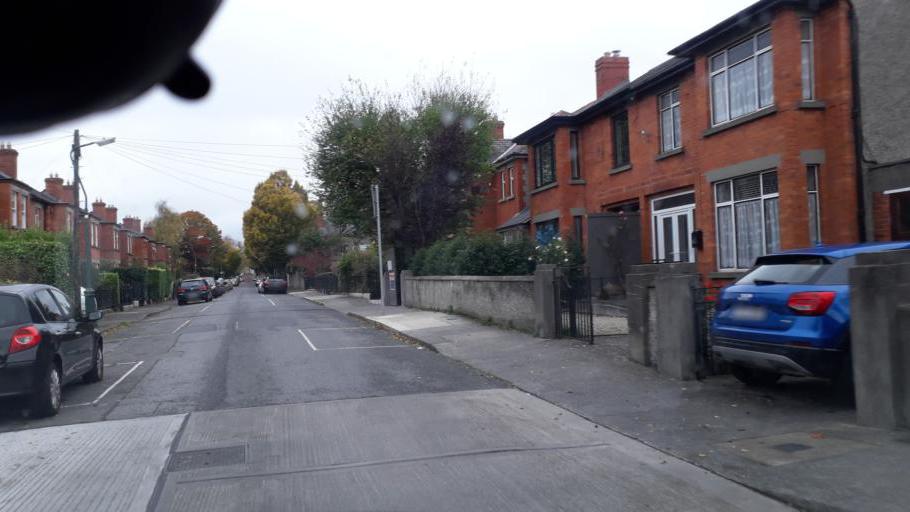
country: IE
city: Milltown
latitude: 53.3186
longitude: -6.2497
